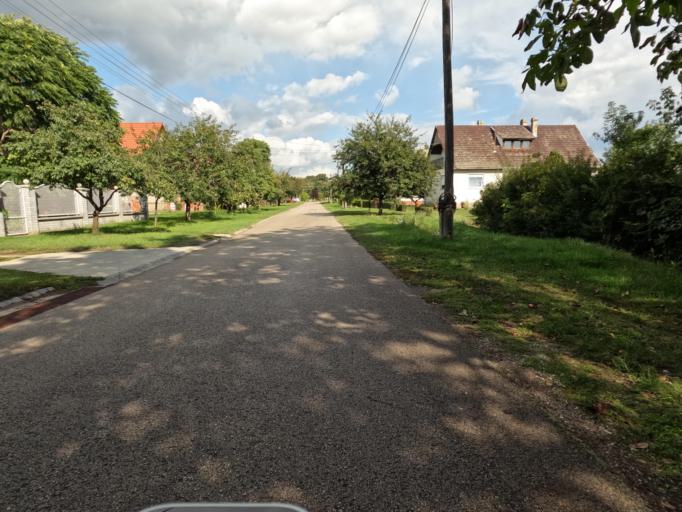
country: HU
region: Tolna
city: Tengelic
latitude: 46.5261
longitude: 18.7082
